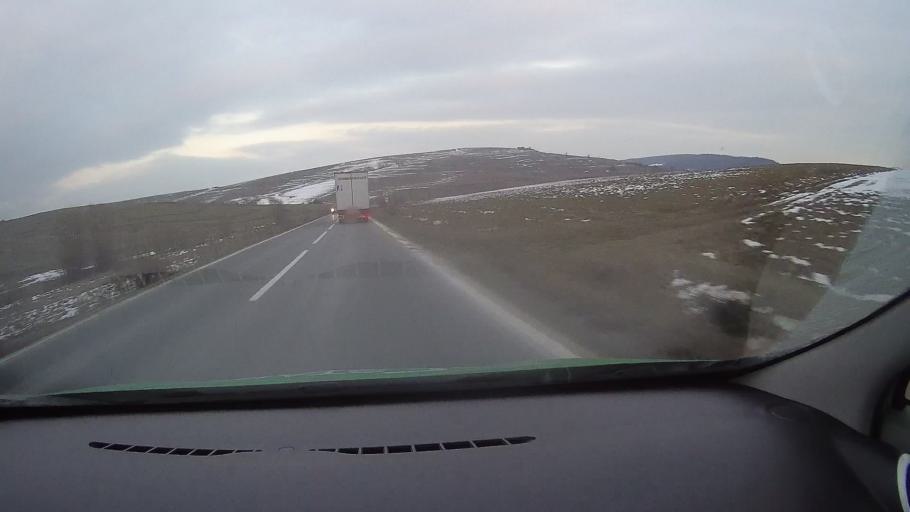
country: RO
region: Harghita
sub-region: Comuna Lupeni
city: Lupeni
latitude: 46.3507
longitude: 25.2594
